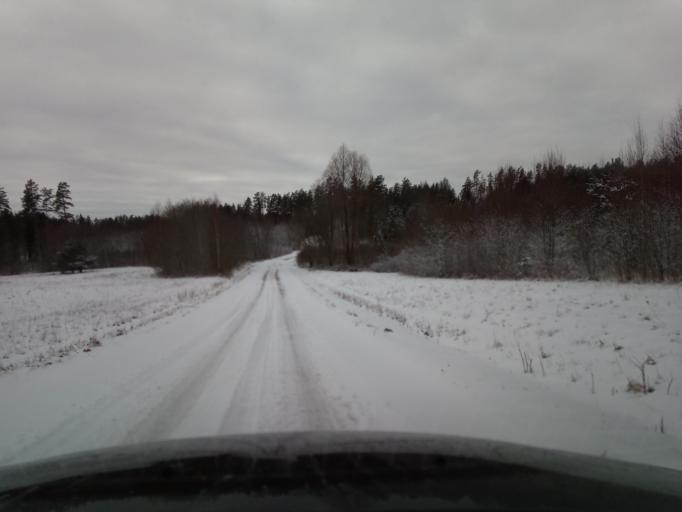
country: LT
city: Zarasai
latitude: 55.6782
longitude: 25.9967
